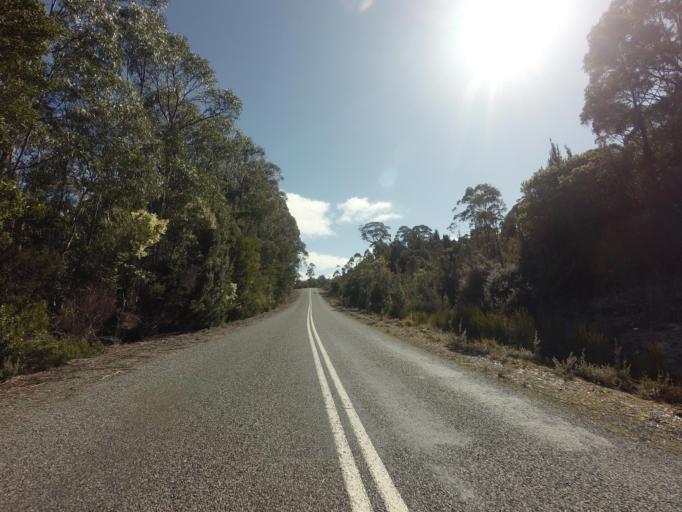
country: AU
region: Tasmania
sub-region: Derwent Valley
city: New Norfolk
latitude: -42.7625
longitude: 146.3965
